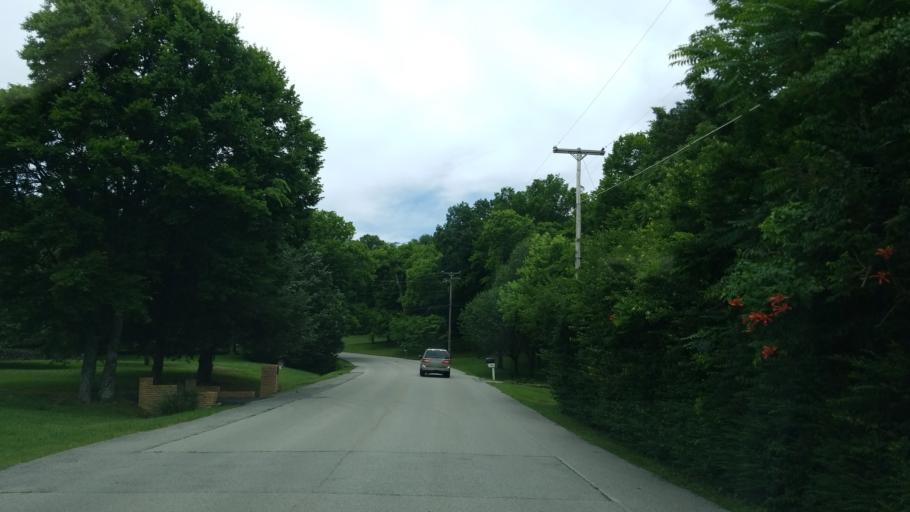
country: US
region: Tennessee
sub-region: Williamson County
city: Brentwood
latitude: 36.0389
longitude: -86.7908
